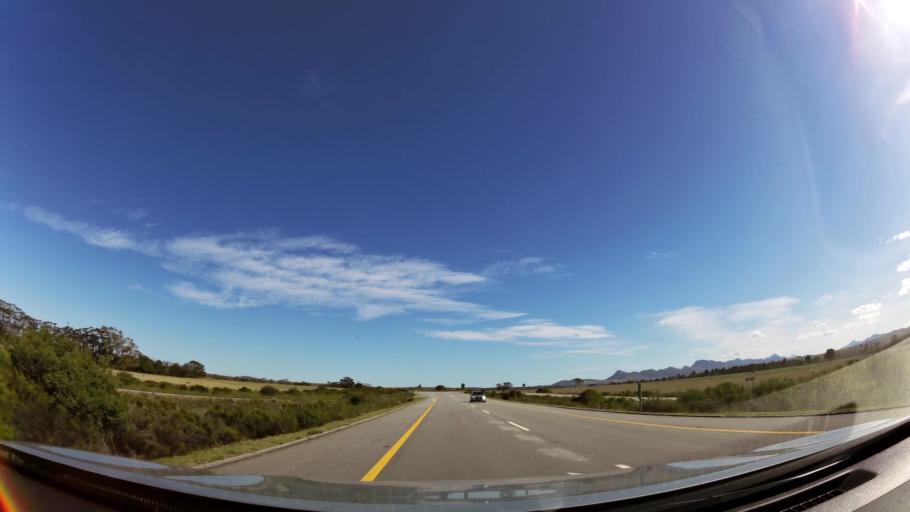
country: ZA
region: Eastern Cape
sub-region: Cacadu District Municipality
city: Kruisfontein
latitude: -34.0297
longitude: 24.5993
